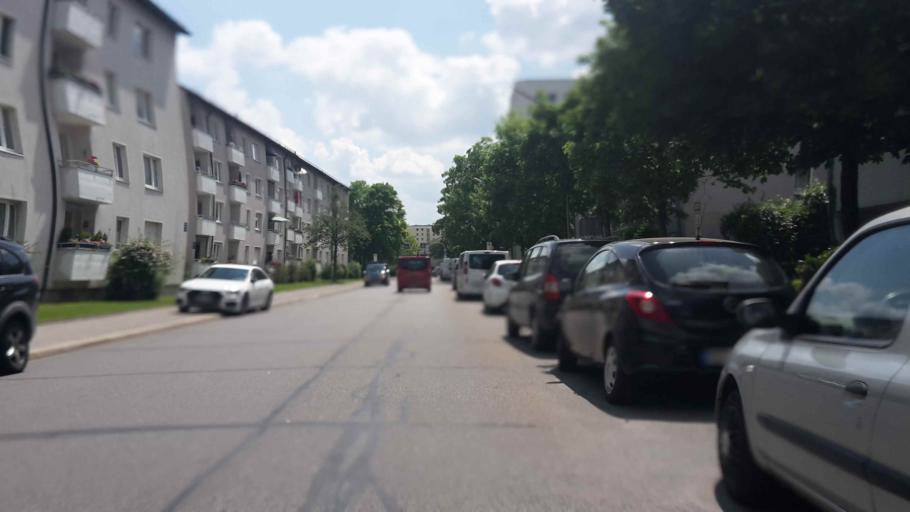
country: DE
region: Bavaria
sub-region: Upper Bavaria
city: Karlsfeld
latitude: 48.1831
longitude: 11.4956
